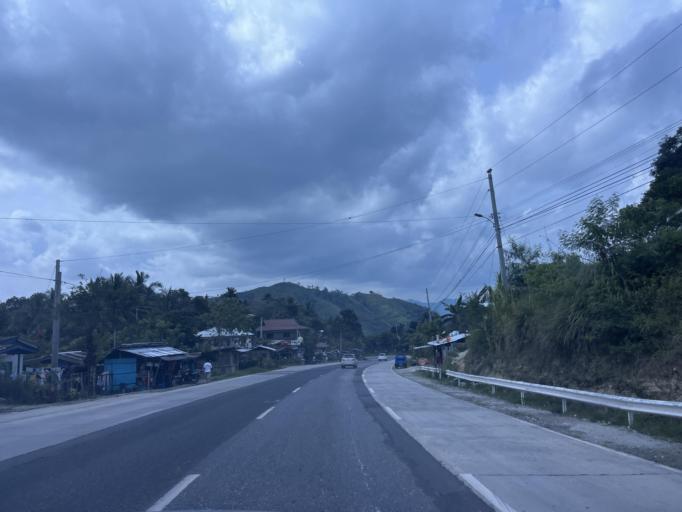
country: PH
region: Davao
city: Simod
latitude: 7.3669
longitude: 125.2838
